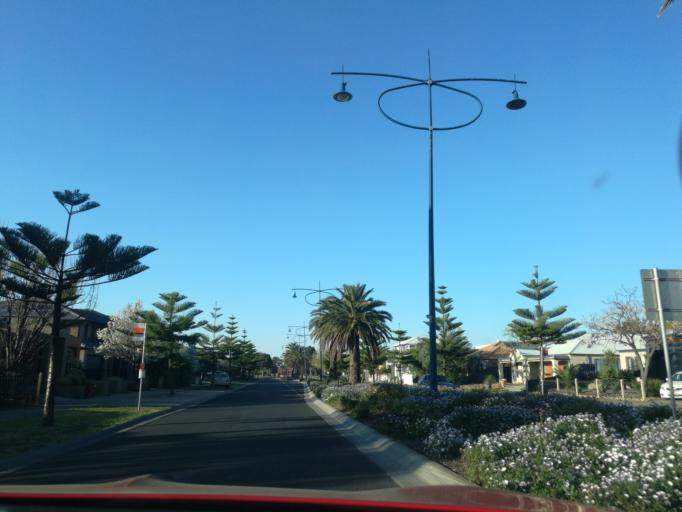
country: AU
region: Victoria
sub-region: Wyndham
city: Williams Landing
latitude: -37.8858
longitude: 144.7415
